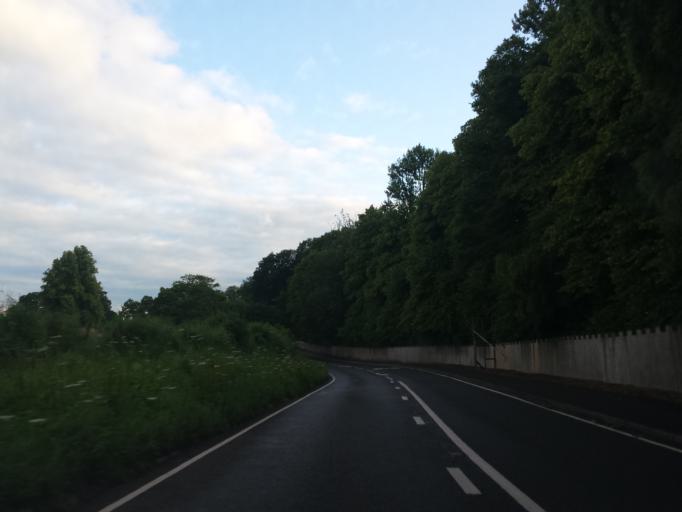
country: GB
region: Scotland
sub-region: Perth and Kinross
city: Scone
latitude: 56.4207
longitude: -3.4256
